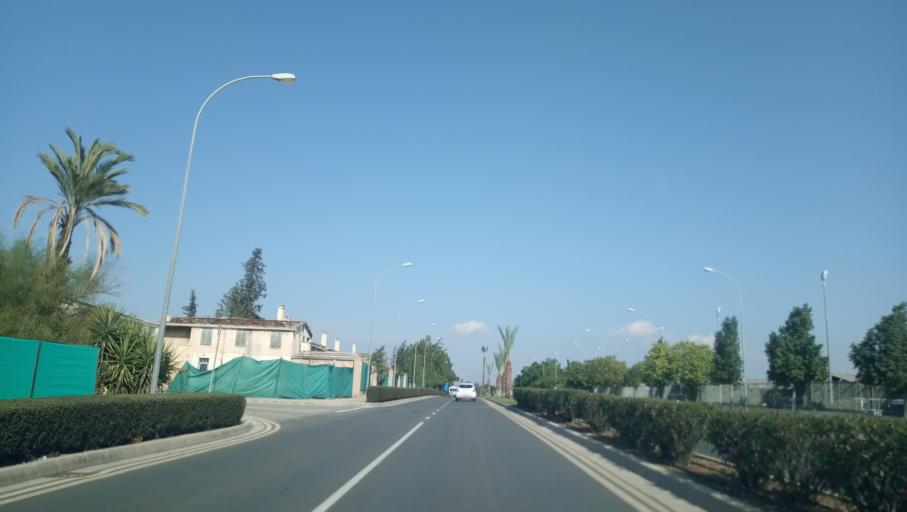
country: CY
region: Lefkosia
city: Nicosia
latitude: 35.1456
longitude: 33.3814
